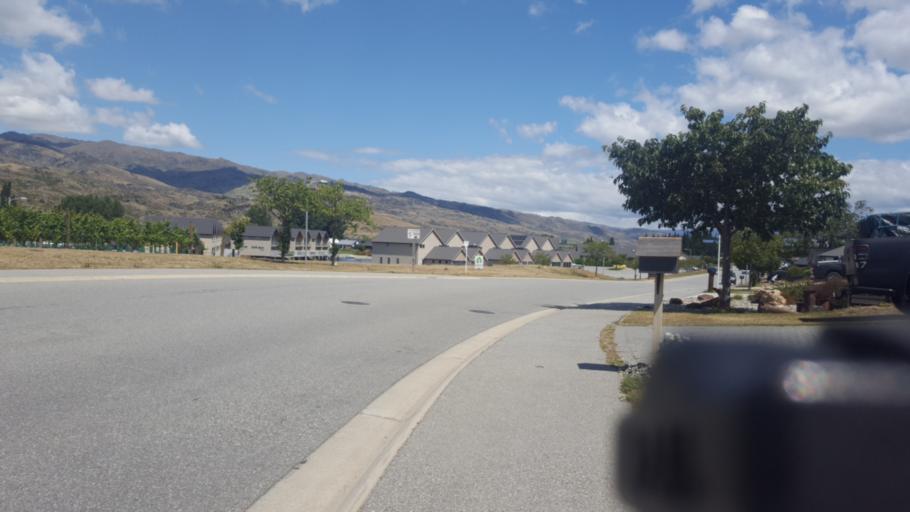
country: NZ
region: Otago
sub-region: Queenstown-Lakes District
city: Wanaka
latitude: -44.9785
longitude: 169.2361
